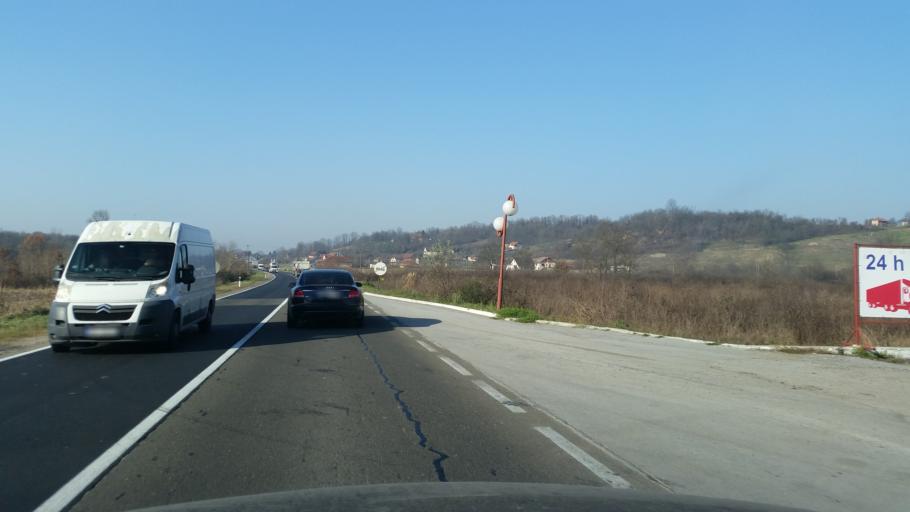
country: RS
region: Central Serbia
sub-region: Belgrade
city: Lazarevac
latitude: 44.3145
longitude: 20.2381
